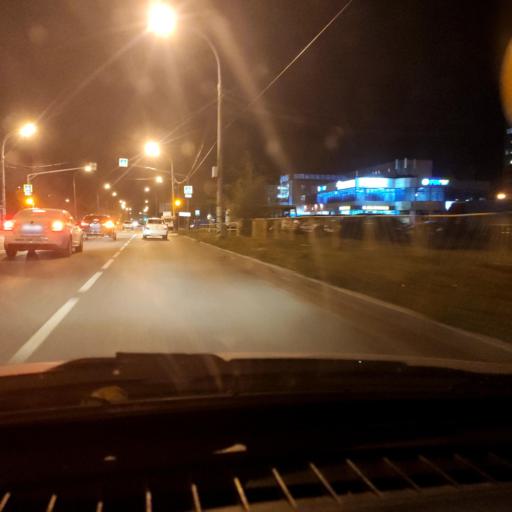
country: RU
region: Samara
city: Tol'yatti
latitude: 53.5439
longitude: 49.3462
